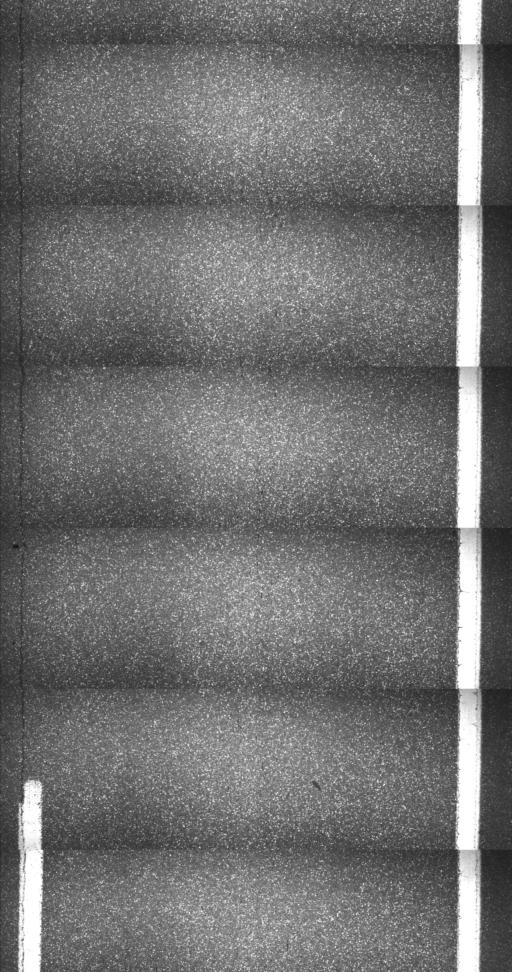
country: US
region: Vermont
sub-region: Windsor County
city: White River Junction
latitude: 43.6598
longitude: -72.3225
